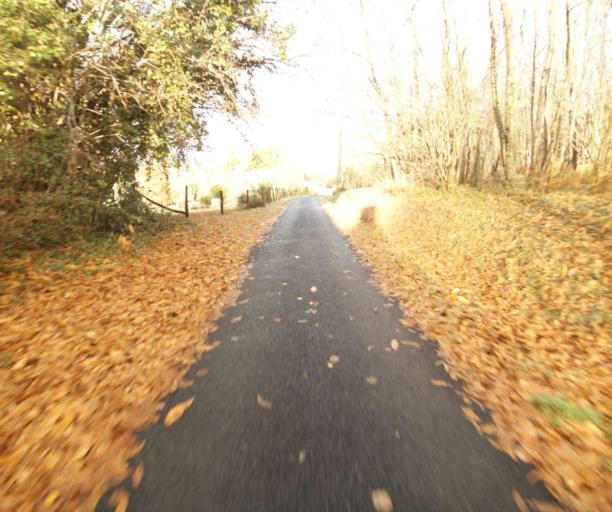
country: FR
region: Limousin
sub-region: Departement de la Correze
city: Saint-Mexant
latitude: 45.2699
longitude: 1.6317
